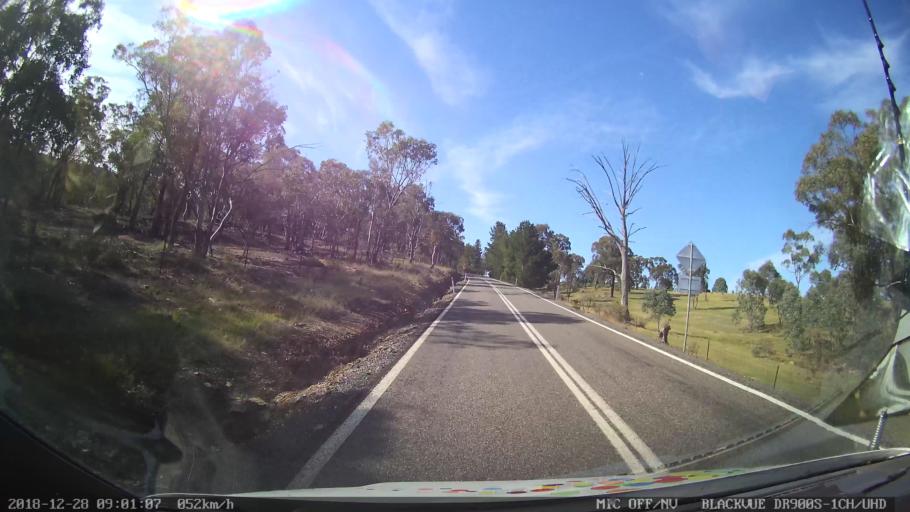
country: AU
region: New South Wales
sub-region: Upper Lachlan Shire
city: Crookwell
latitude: -34.1440
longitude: 149.3333
